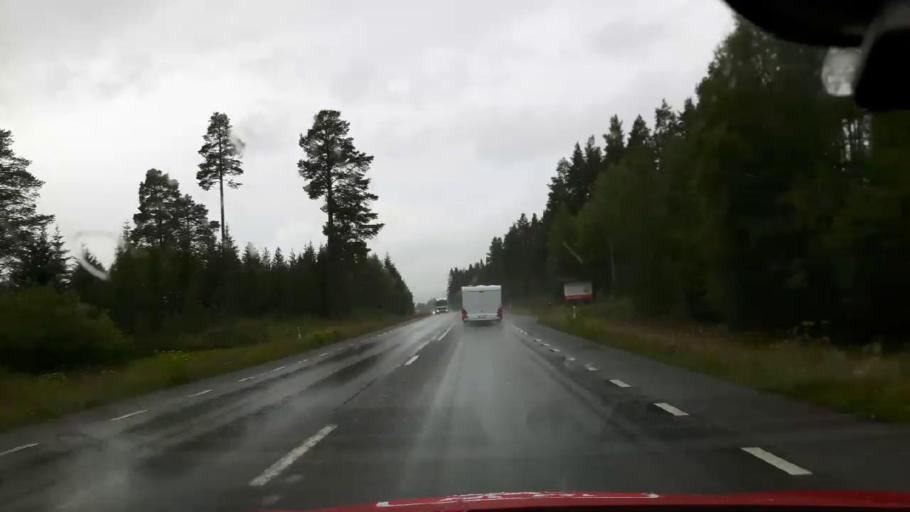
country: SE
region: Jaemtland
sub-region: Are Kommun
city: Jarpen
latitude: 63.3393
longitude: 13.4940
